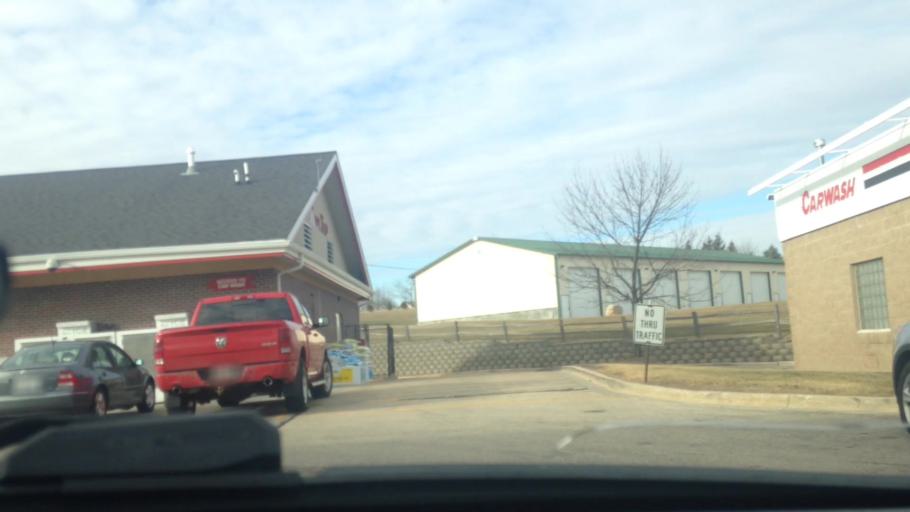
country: US
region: Wisconsin
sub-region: Washington County
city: Slinger
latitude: 43.3253
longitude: -88.2597
